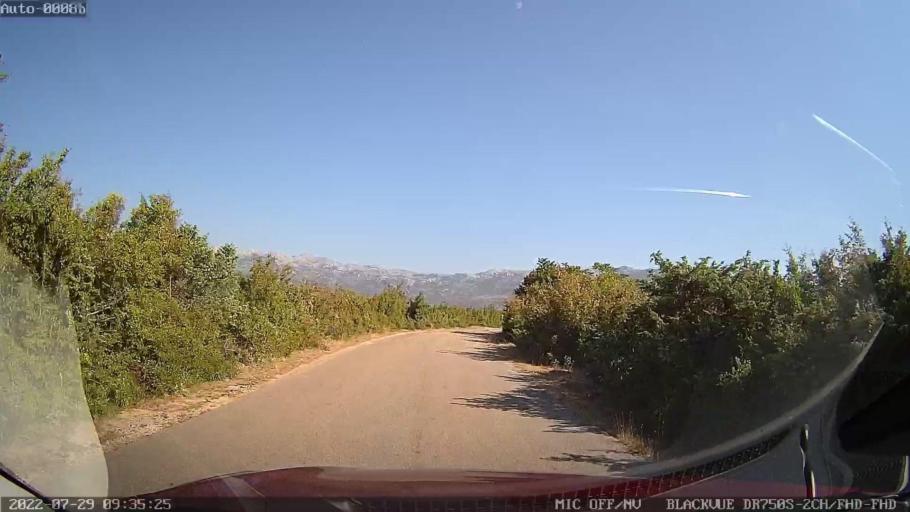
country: HR
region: Zadarska
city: Obrovac
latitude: 44.1856
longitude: 15.7324
